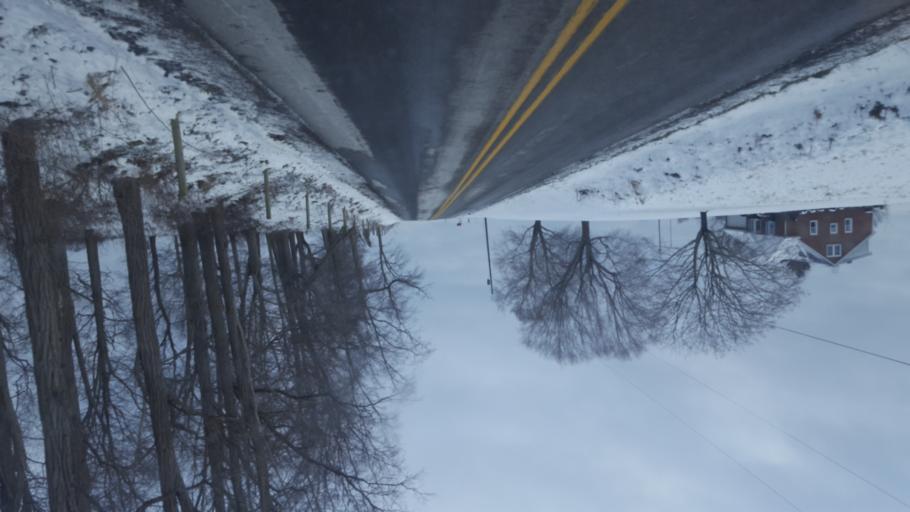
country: US
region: Pennsylvania
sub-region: Lawrence County
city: New Wilmington
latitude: 41.1471
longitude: -80.2699
